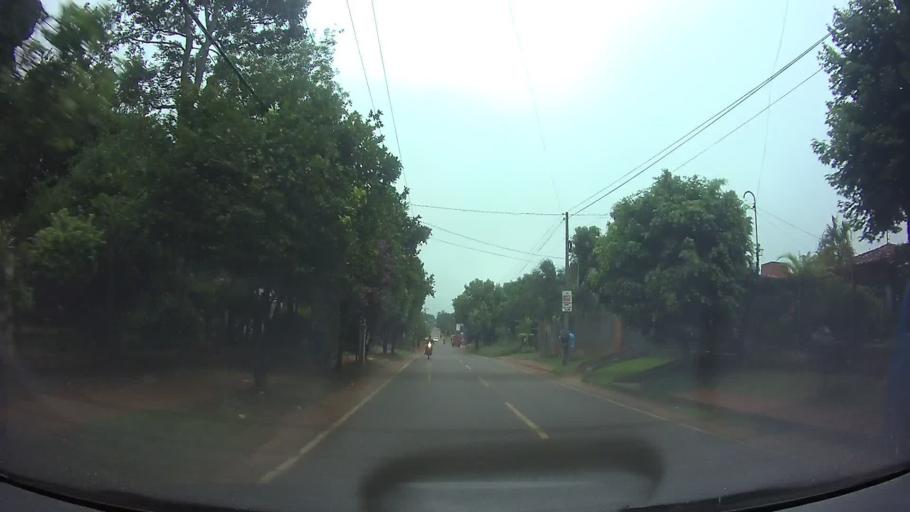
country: PY
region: Central
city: Itaugua
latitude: -25.3855
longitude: -57.3509
